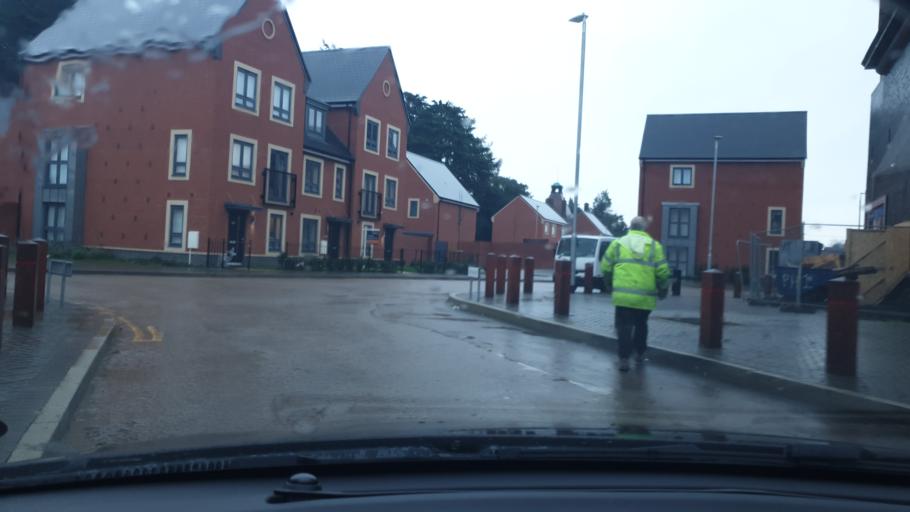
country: GB
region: England
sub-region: Essex
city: Great Horkesley
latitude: 51.9190
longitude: 0.8951
